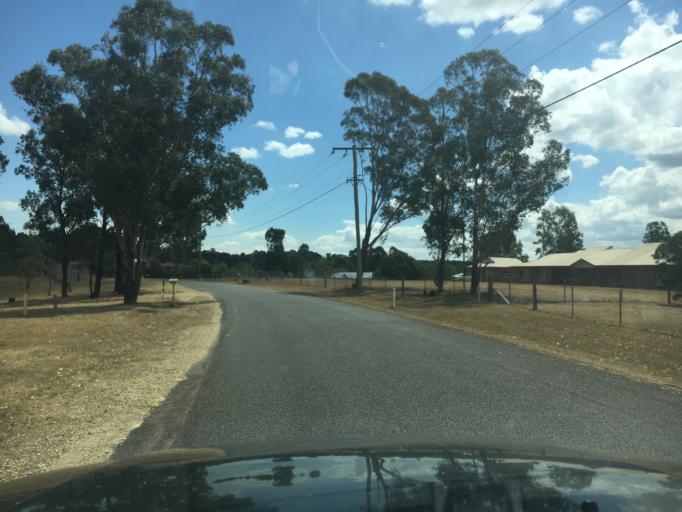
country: AU
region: New South Wales
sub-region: Singleton
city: Singleton
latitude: -32.5200
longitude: 151.1888
